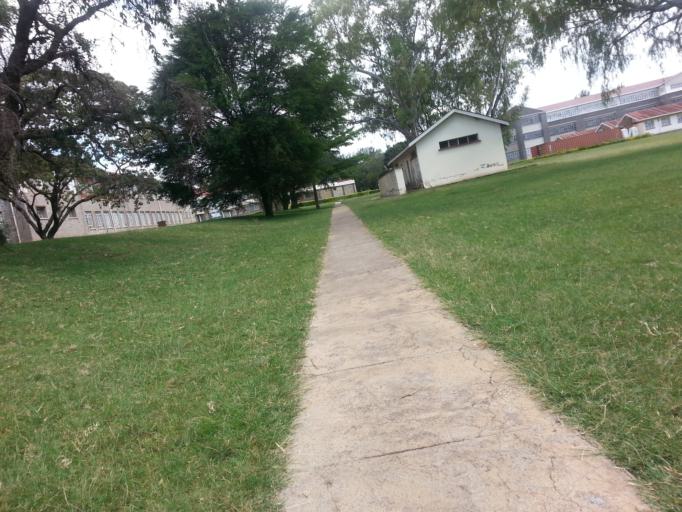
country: KE
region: Nakuru
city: Rongai
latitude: -0.1677
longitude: 35.9651
